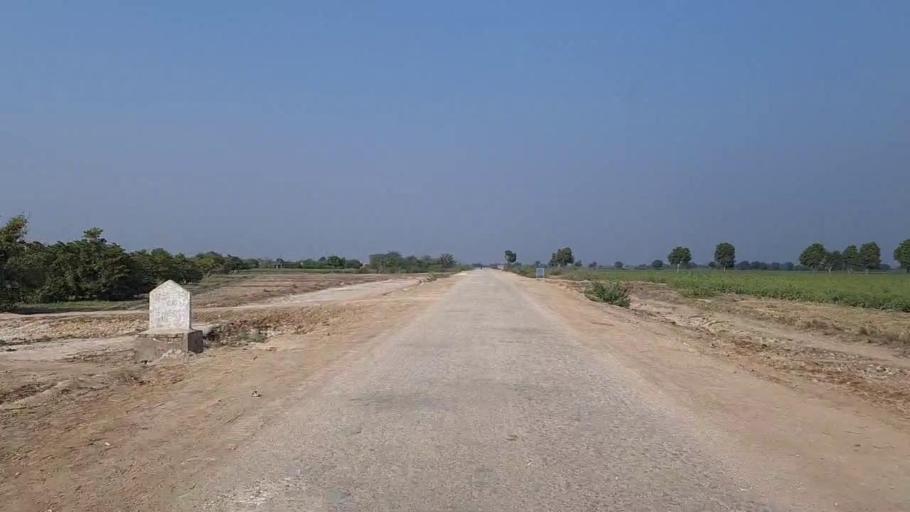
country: PK
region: Sindh
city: Mirwah Gorchani
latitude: 25.4025
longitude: 69.1398
